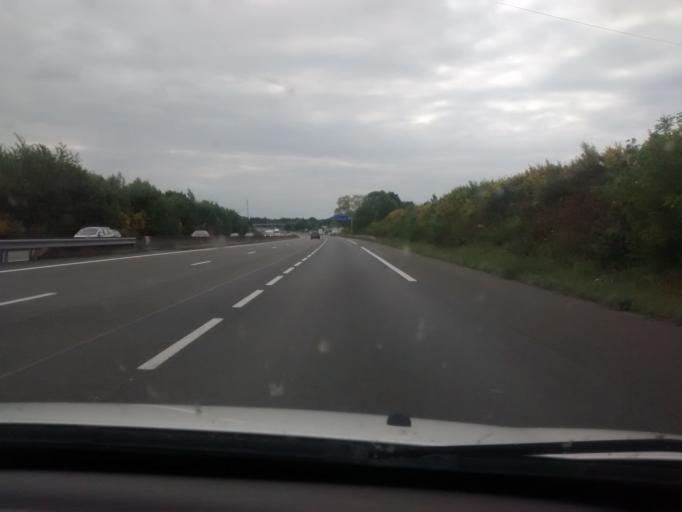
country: FR
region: Pays de la Loire
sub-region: Departement de la Sarthe
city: Sarge-les-le-Mans
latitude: 48.0530
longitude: 0.2621
